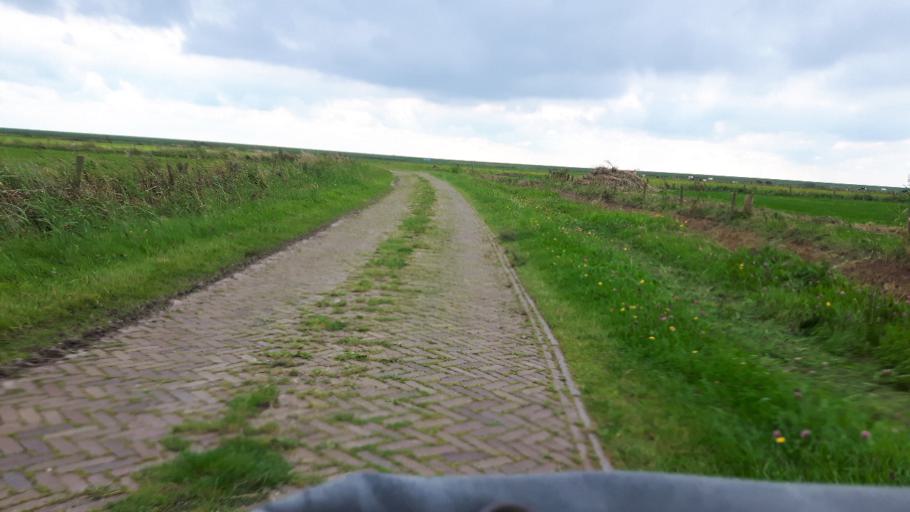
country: NL
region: Friesland
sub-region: Gemeente Ameland
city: Nes
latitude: 53.4471
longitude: 5.8195
